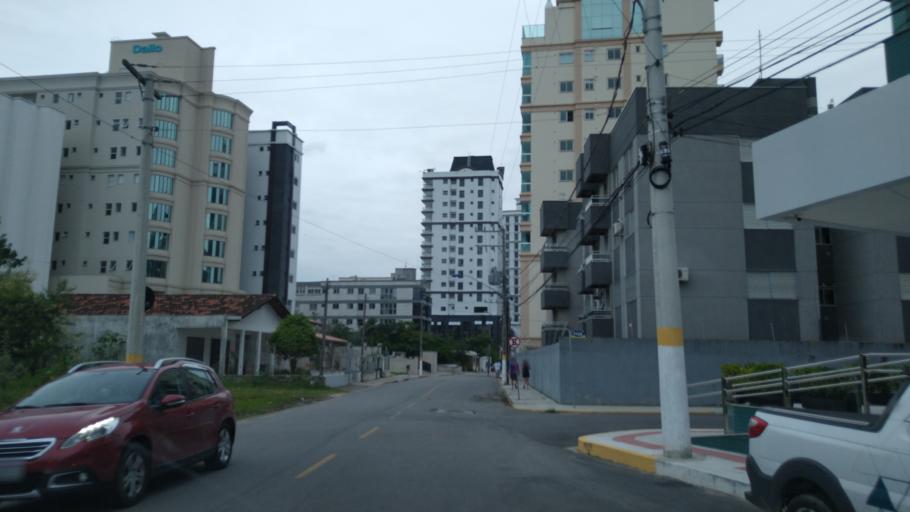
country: BR
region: Santa Catarina
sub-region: Itapema
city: Itapema
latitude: -27.0926
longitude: -48.6118
